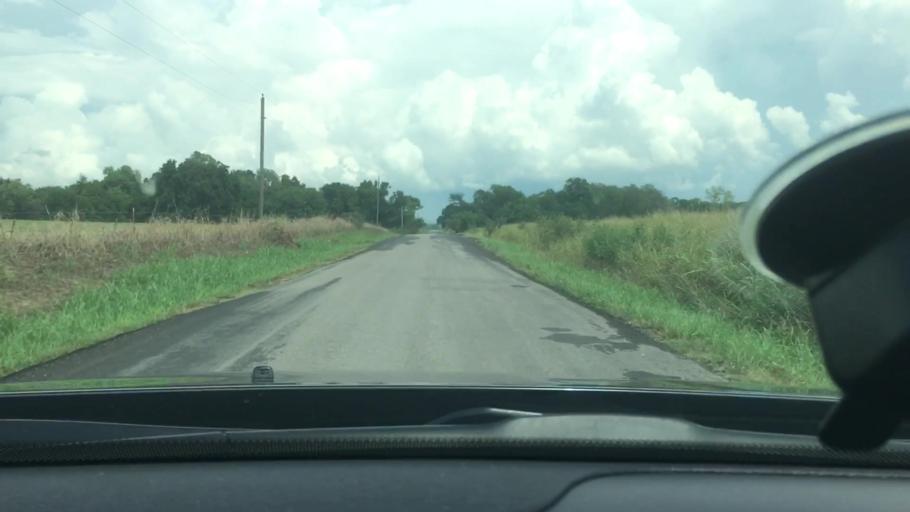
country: US
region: Oklahoma
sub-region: Carter County
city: Dickson
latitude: 34.2118
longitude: -96.8982
